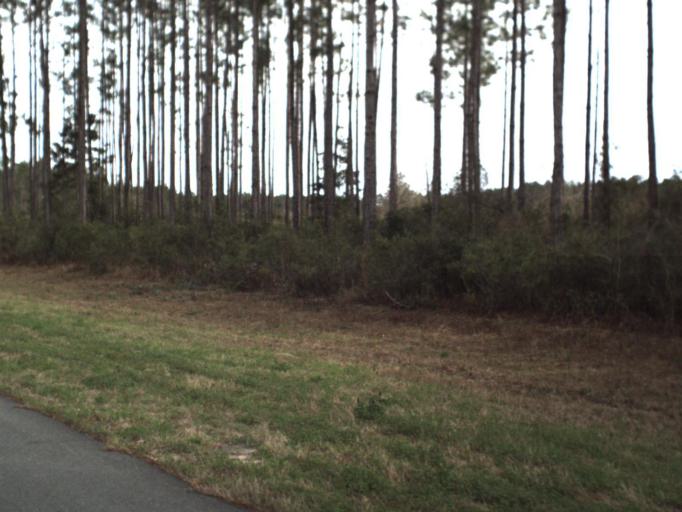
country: US
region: Florida
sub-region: Bay County
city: Callaway
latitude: 30.1437
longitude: -85.4276
